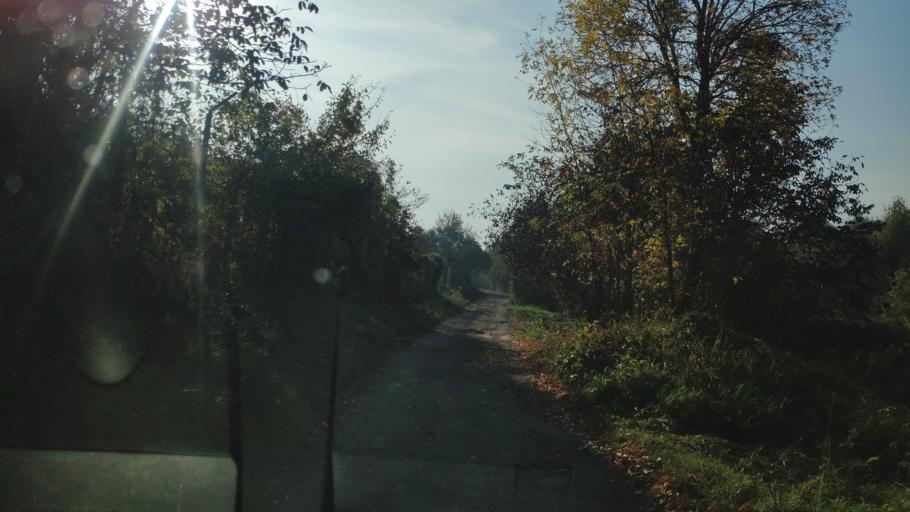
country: SK
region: Kosicky
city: Kosice
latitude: 48.7286
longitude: 21.2230
